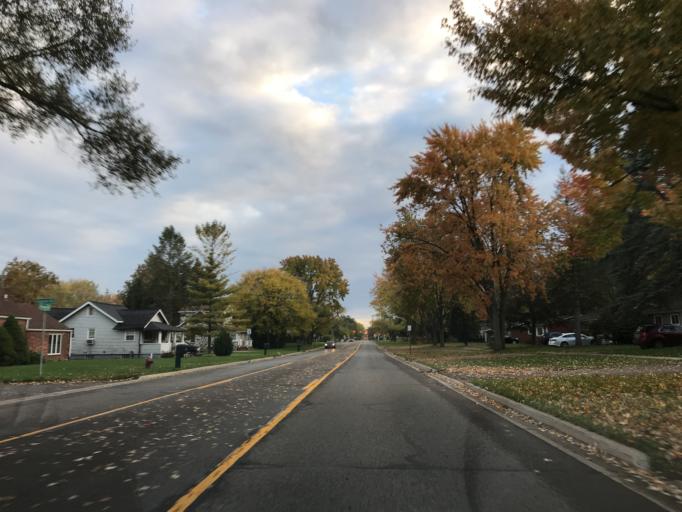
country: US
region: Michigan
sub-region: Oakland County
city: Farmington
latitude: 42.4531
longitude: -83.3174
